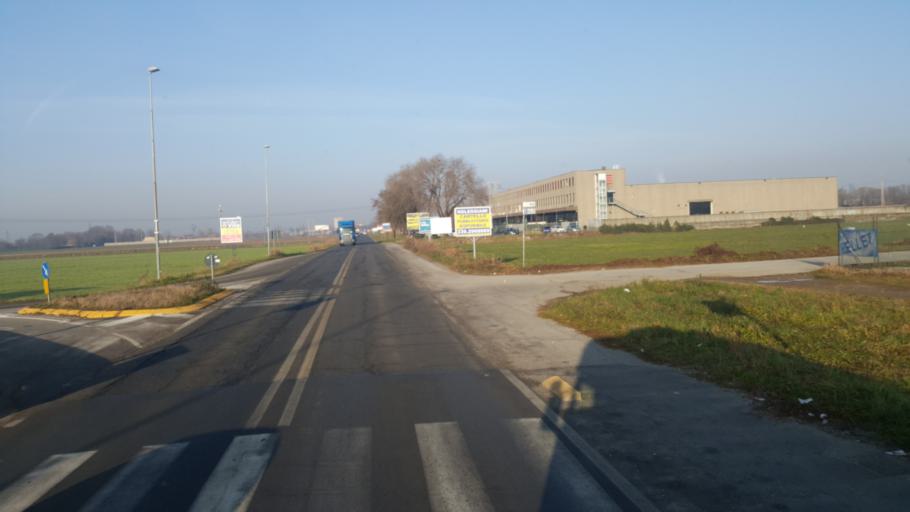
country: IT
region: Lombardy
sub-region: Citta metropolitana di Milano
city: Cassano d'Adda
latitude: 45.5302
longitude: 9.5019
